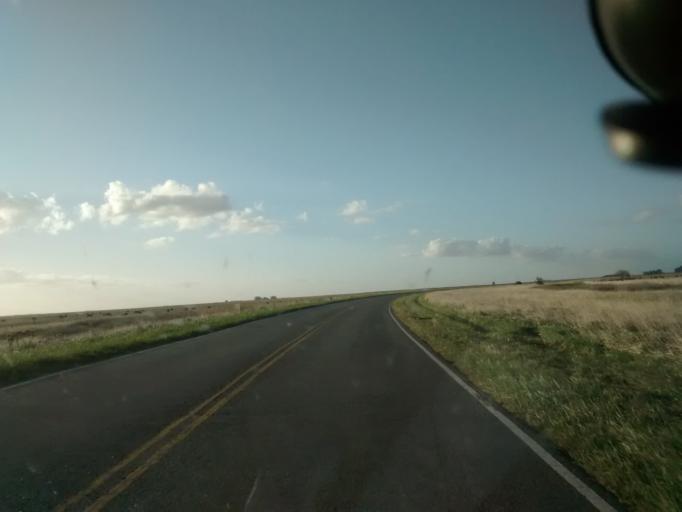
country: AR
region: Buenos Aires
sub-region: Partido de General Belgrano
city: General Belgrano
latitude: -36.0705
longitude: -58.6248
